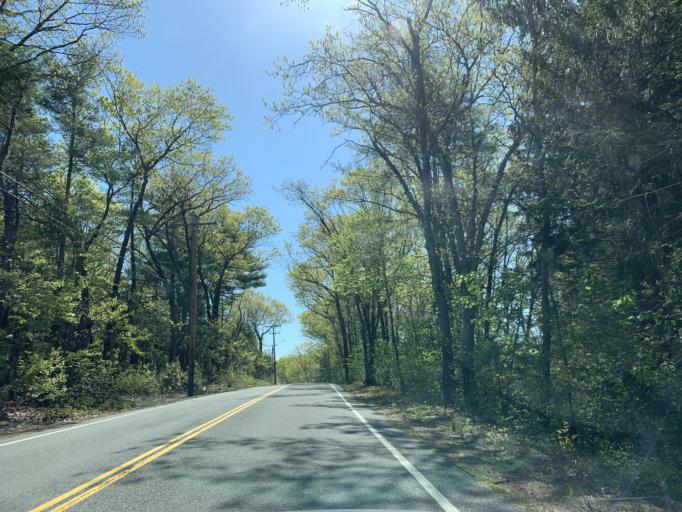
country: US
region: Massachusetts
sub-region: Middlesex County
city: West Concord
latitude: 42.4179
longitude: -71.3936
